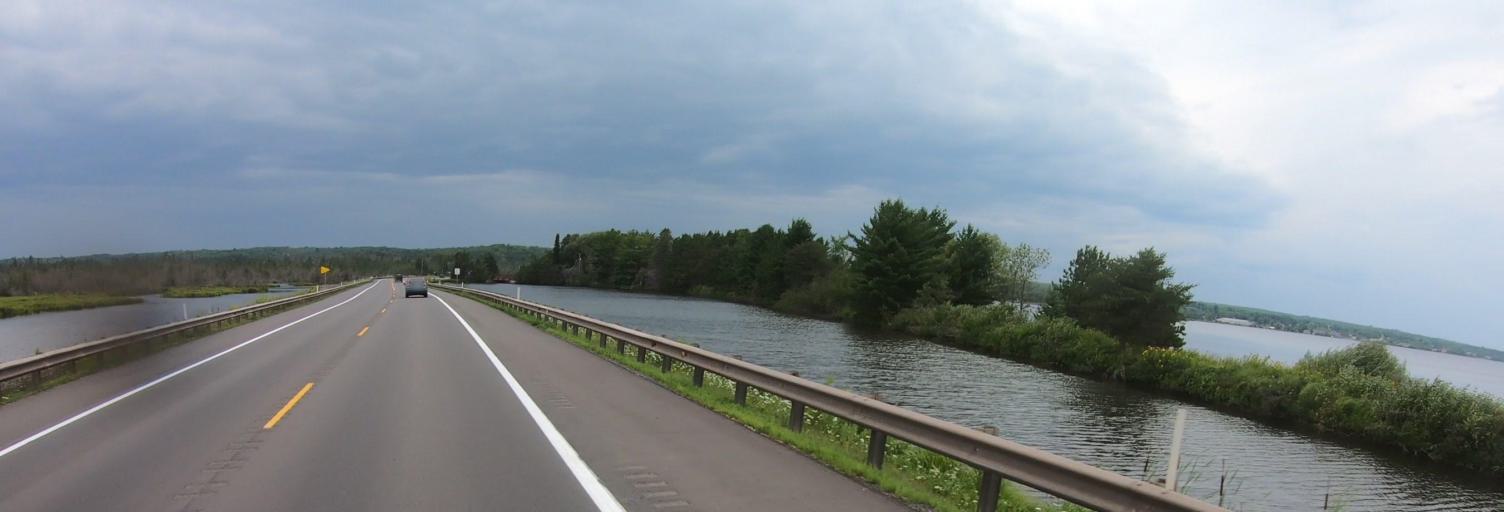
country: US
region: Michigan
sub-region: Baraga County
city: Baraga
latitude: 46.7545
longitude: -88.4888
